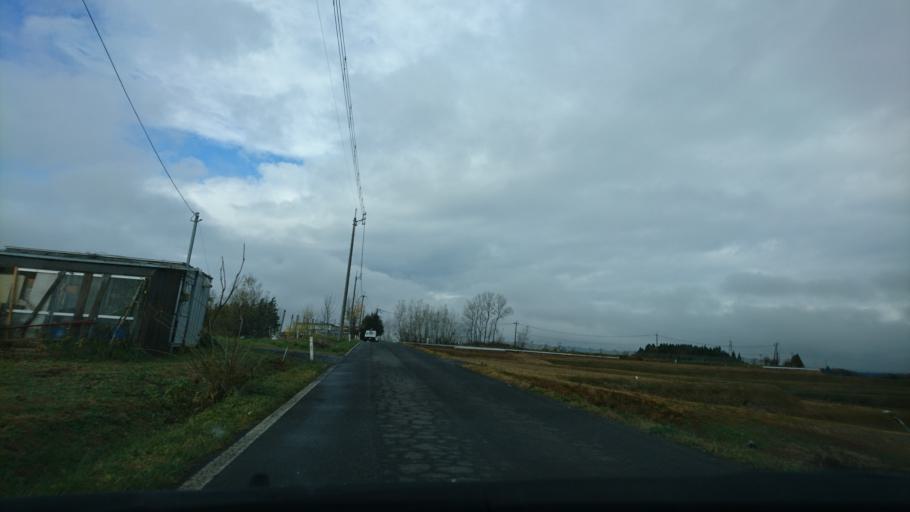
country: JP
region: Iwate
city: Ichinoseki
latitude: 38.8872
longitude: 141.1933
